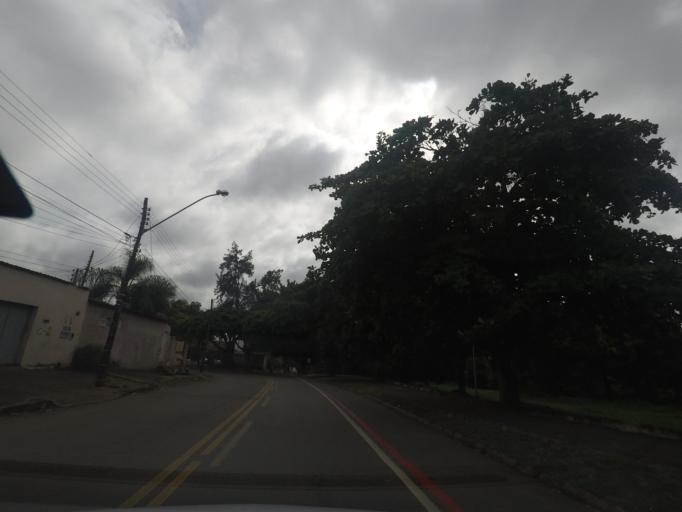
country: BR
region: Goias
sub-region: Goiania
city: Goiania
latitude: -16.7265
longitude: -49.2586
